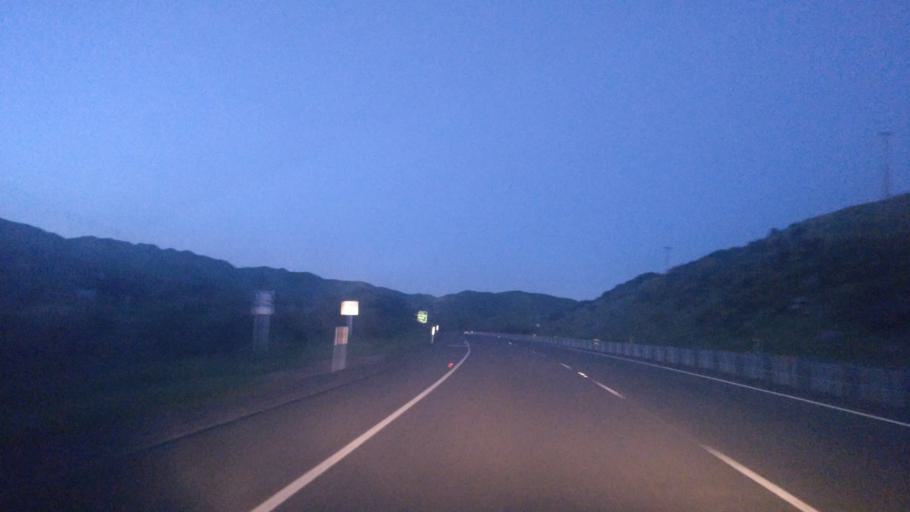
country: NZ
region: Wellington
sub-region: Porirua City
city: Porirua
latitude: -41.0689
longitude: 174.8769
